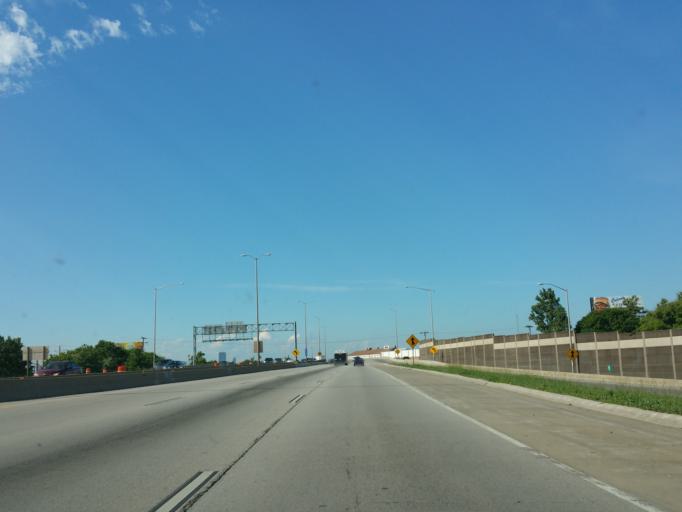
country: US
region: Wisconsin
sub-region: Milwaukee County
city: Saint Francis
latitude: 42.9836
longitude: -87.9160
